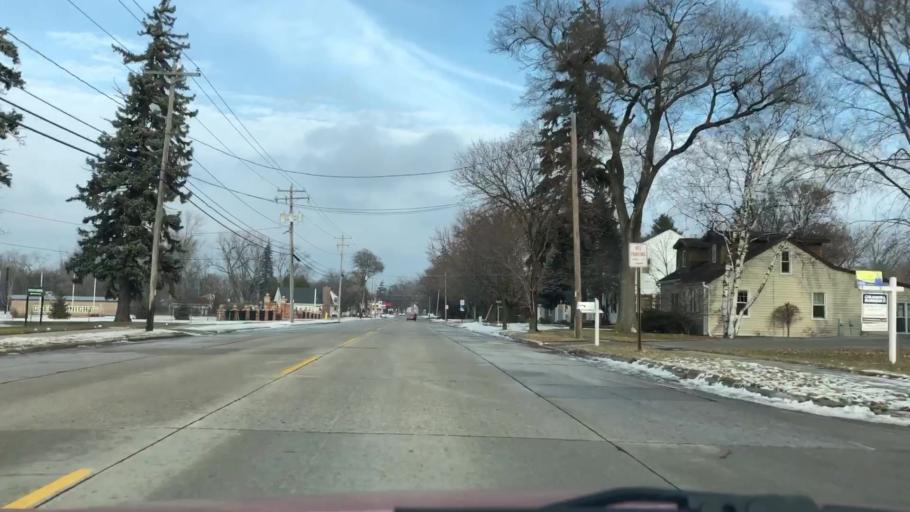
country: US
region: Wisconsin
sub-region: Brown County
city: De Pere
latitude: 44.4350
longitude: -88.0741
